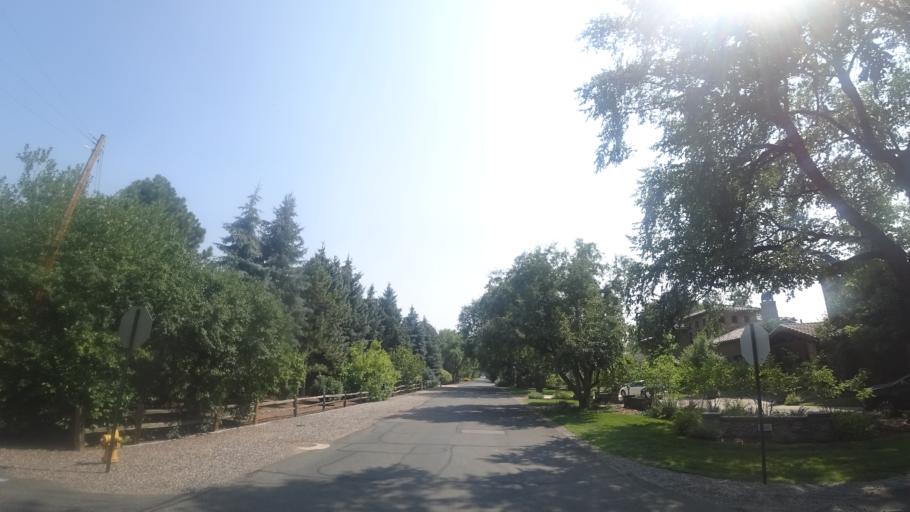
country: US
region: Colorado
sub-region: Arapahoe County
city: Cherry Hills Village
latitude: 39.6333
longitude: -104.9691
